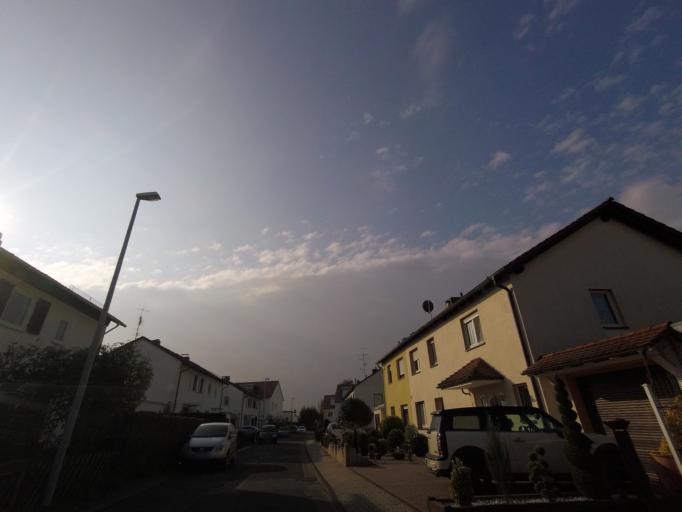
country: DE
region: Hesse
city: Schwalbach am Taunus
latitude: 50.1460
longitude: 8.5418
